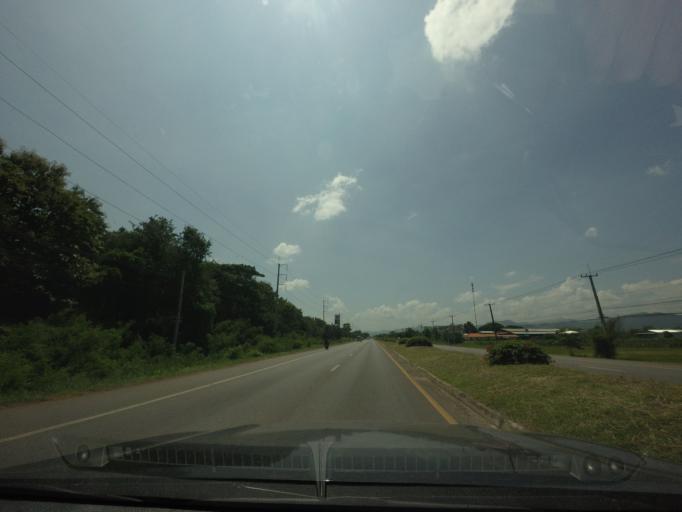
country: TH
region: Phetchabun
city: Lom Sak
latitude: 16.7179
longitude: 101.1821
